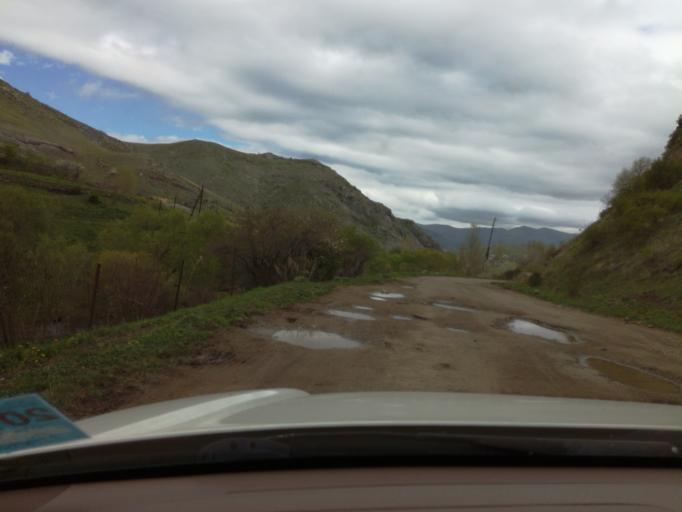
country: AM
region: Lorri
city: Lerrnapat
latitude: 40.8074
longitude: 44.3819
